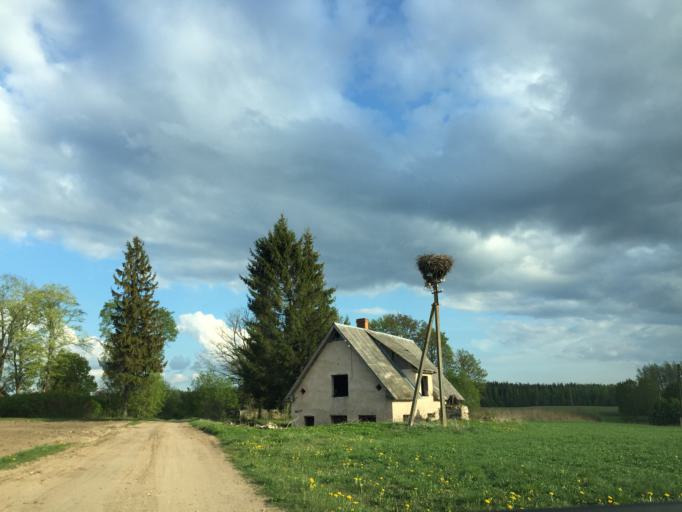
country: LV
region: Limbazu Rajons
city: Limbazi
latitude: 57.3686
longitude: 24.7653
